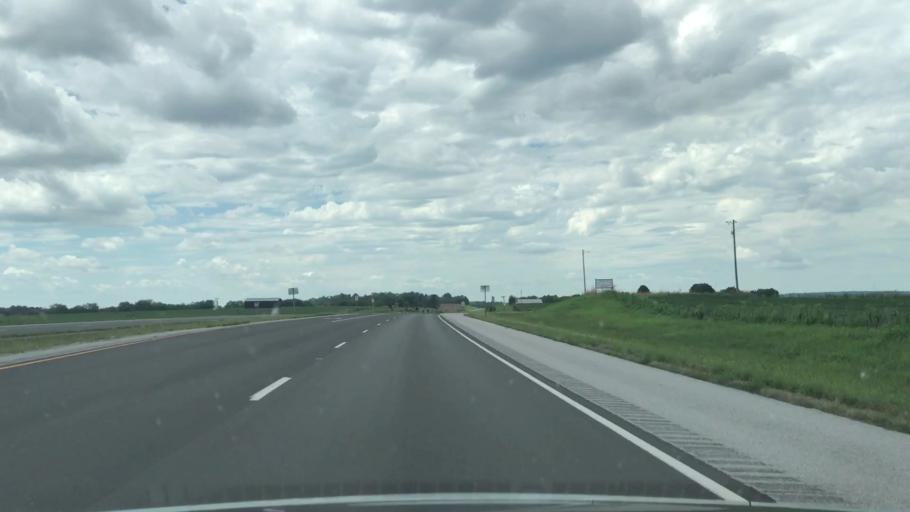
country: US
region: Kentucky
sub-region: Logan County
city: Russellville
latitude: 36.8264
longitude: -86.9840
